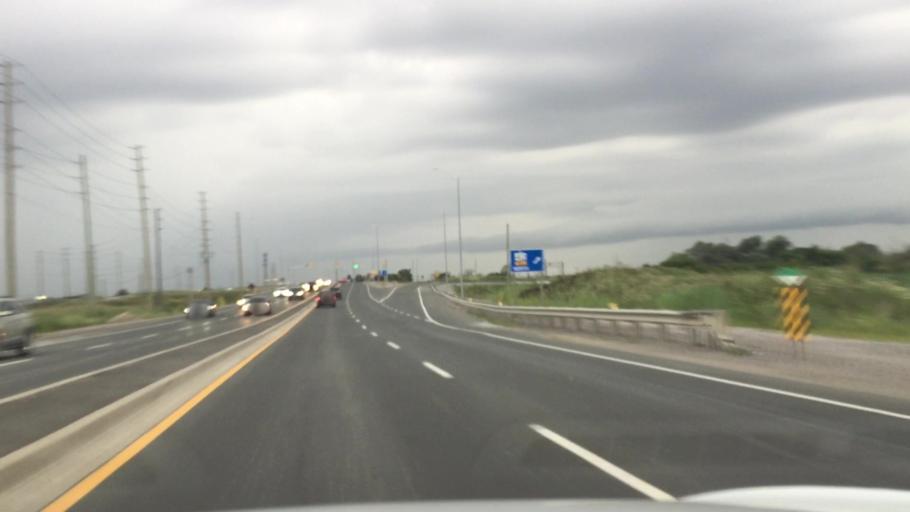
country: CA
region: Ontario
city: Ajax
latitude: 43.9074
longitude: -78.9910
